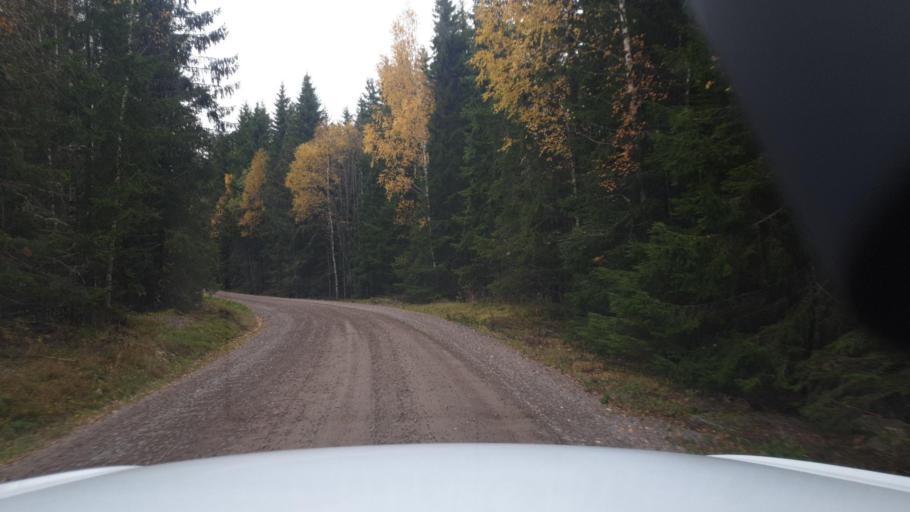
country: SE
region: Vaermland
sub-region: Arvika Kommun
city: Arvika
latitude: 59.9688
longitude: 12.6602
